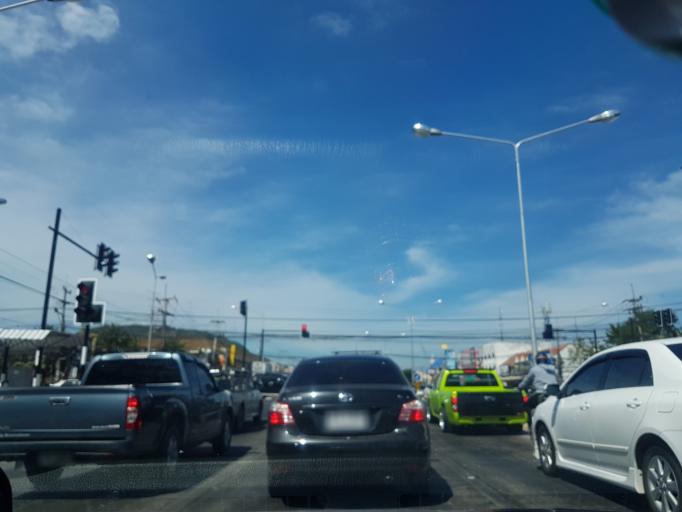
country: TH
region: Chon Buri
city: Sattahip
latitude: 12.6893
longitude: 100.9784
